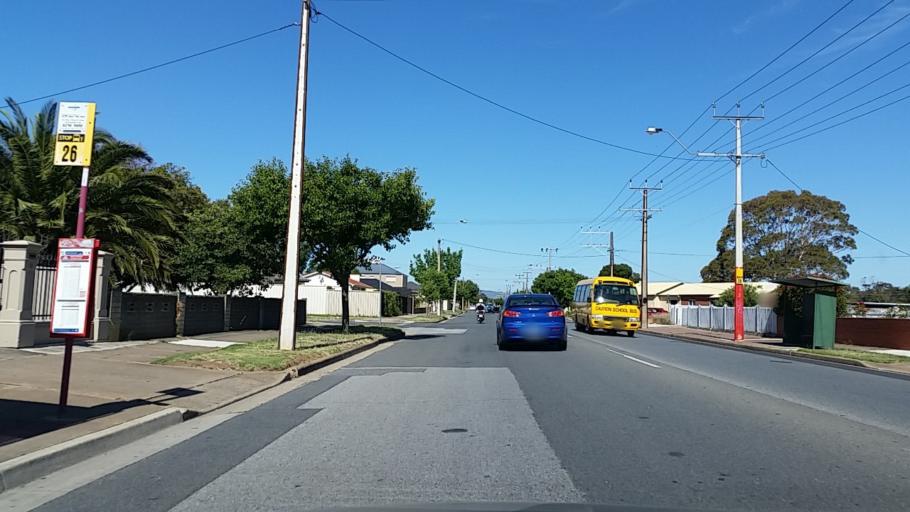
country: AU
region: South Australia
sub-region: Charles Sturt
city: Woodville West
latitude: -34.8913
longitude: 138.5244
